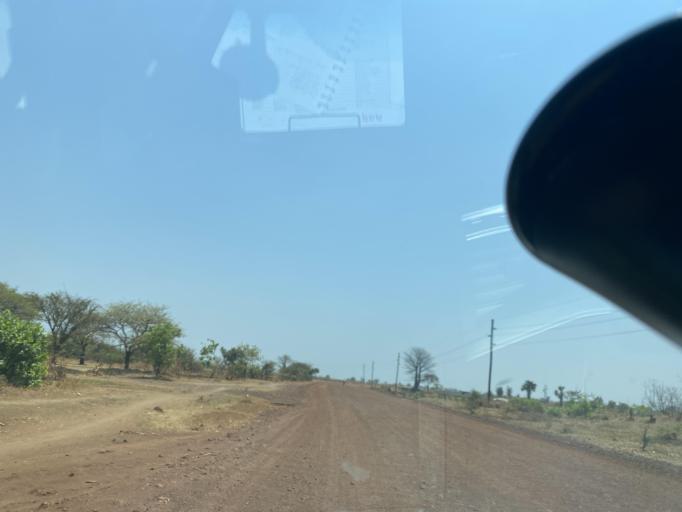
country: ZM
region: Southern
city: Nakambala
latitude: -15.4752
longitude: 27.8973
